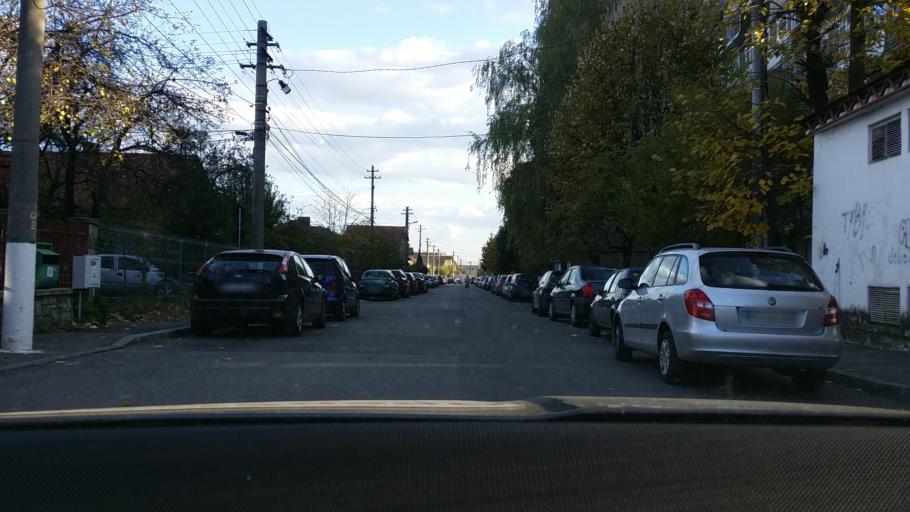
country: RO
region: Prahova
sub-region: Municipiul Campina
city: Campina
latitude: 45.1279
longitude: 25.7424
